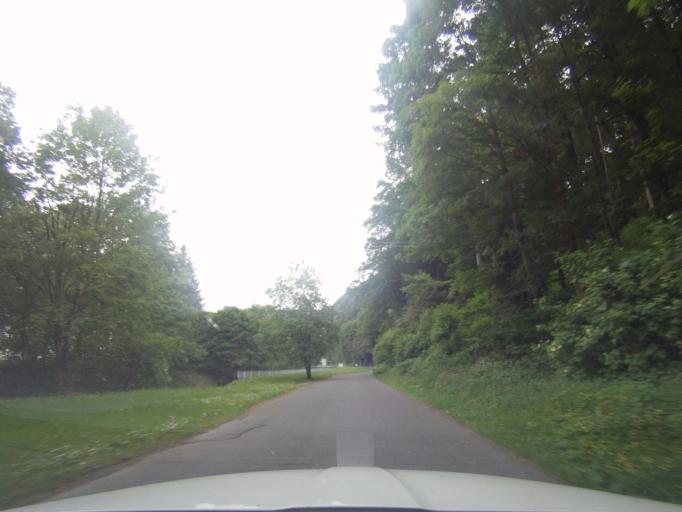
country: DE
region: Thuringia
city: Frauenwald
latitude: 50.5393
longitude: 10.8801
